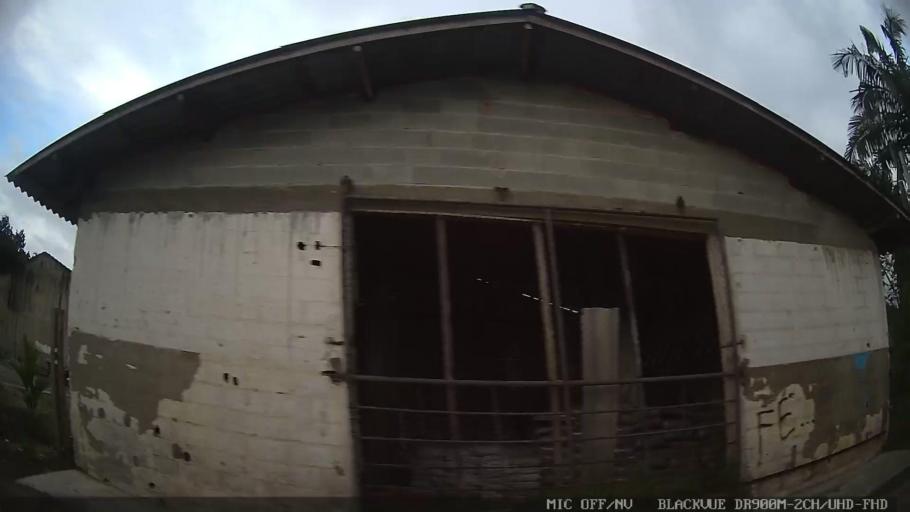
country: BR
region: Sao Paulo
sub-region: Itanhaem
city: Itanhaem
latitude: -24.0902
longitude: -46.7969
